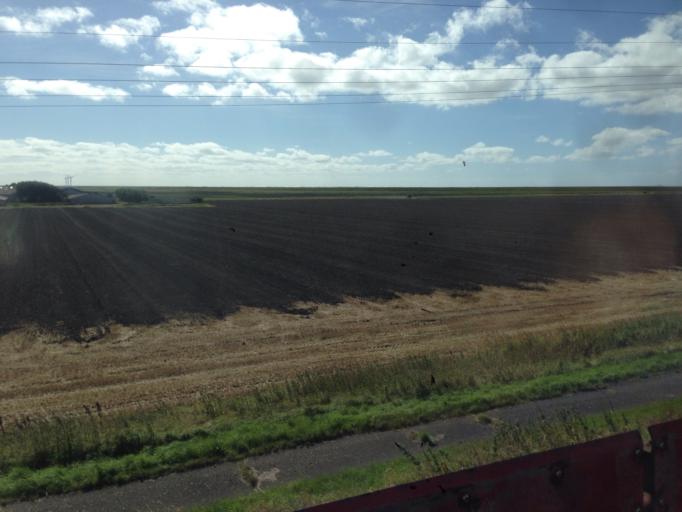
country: DE
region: Schleswig-Holstein
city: Friedrich-Wilhelm-Lubke-Koog
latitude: 54.8867
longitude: 8.6209
